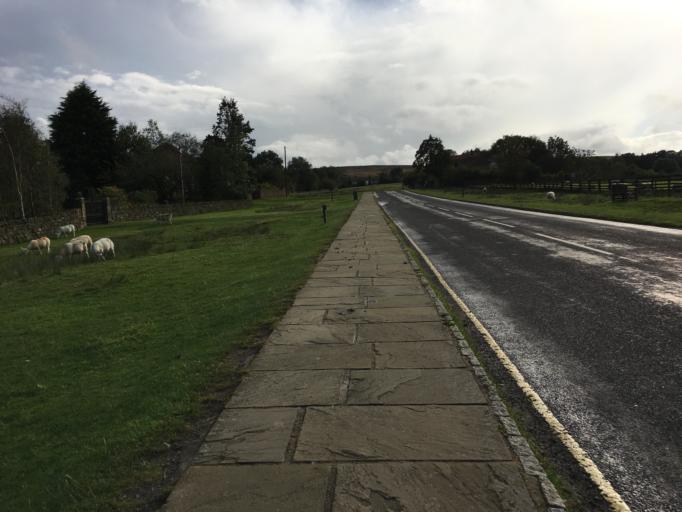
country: GB
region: England
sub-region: North Yorkshire
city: Sleights
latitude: 54.3986
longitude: -0.7219
